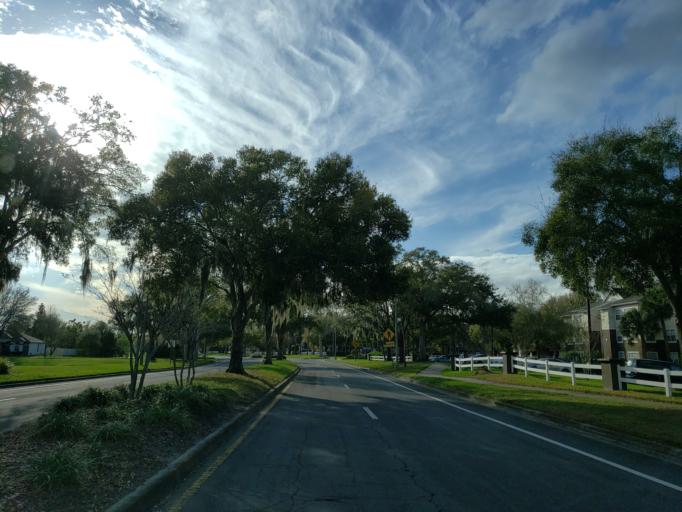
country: US
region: Florida
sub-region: Hillsborough County
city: Riverview
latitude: 27.9078
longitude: -82.3194
